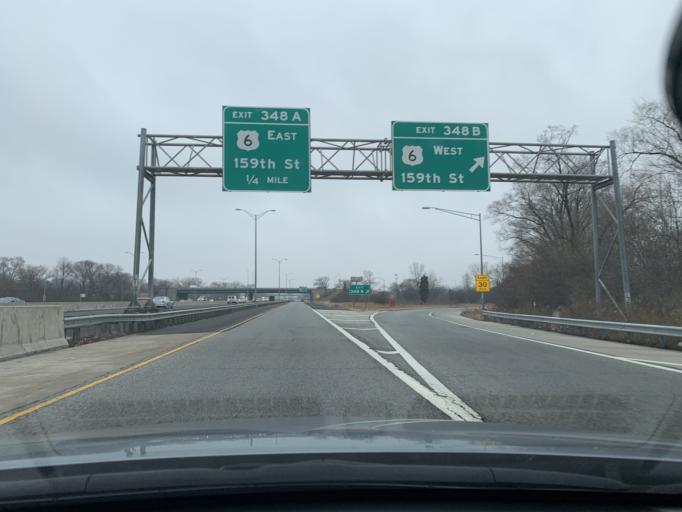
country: US
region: Illinois
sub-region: Cook County
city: Markham
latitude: 41.6038
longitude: -87.7068
